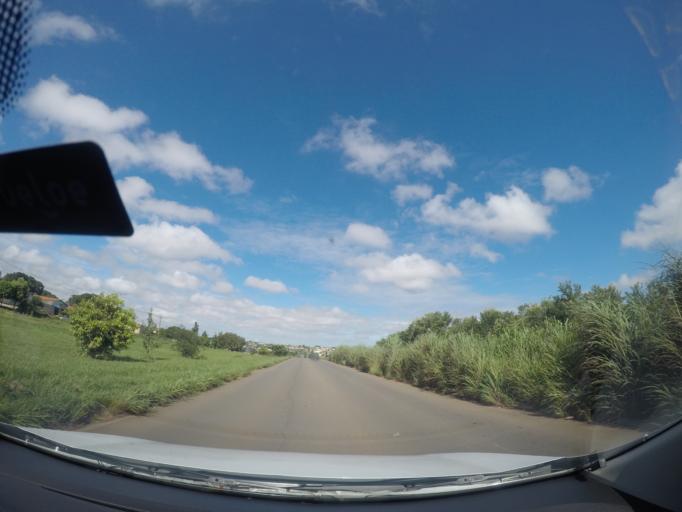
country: BR
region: Goias
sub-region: Senador Canedo
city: Senador Canedo
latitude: -16.6497
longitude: -49.1599
